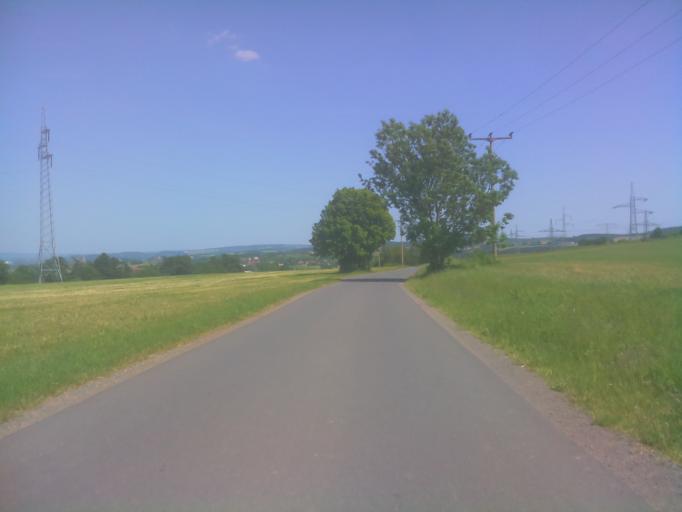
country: DE
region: Thuringia
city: Kaulsdorf
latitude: 50.6393
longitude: 11.4295
